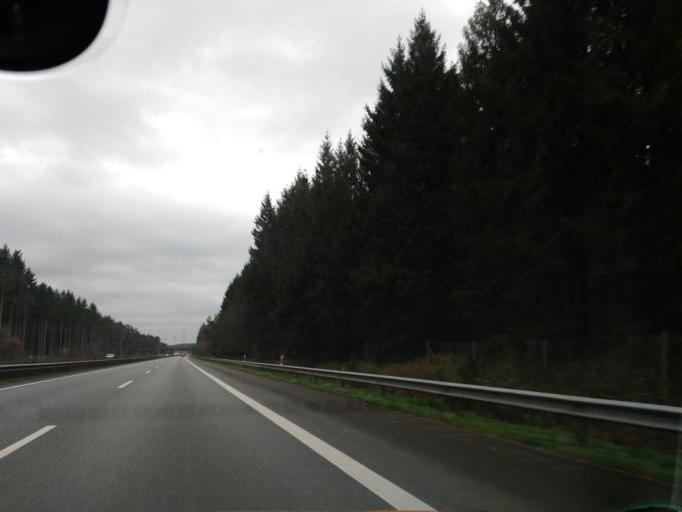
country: DE
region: Lower Saxony
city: Hauslingen
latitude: 52.8980
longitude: 9.4211
